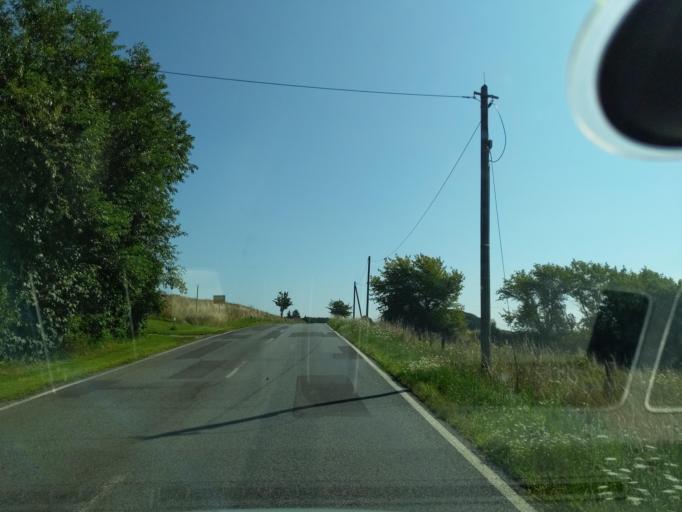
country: DE
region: Saxony
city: Lobau
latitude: 51.1226
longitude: 14.6553
